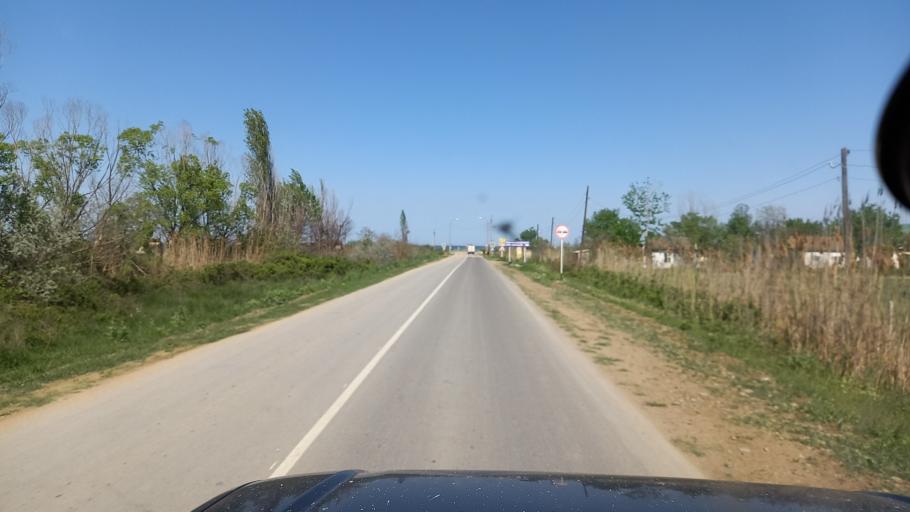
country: RU
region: Dagestan
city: Khazar
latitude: 41.9505
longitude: 48.3596
